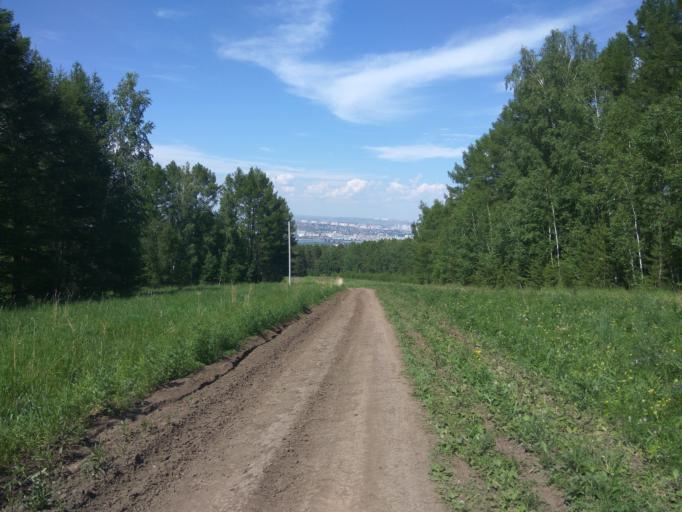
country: RU
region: Krasnoyarskiy
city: Krasnoyarsk
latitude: 55.9564
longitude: 92.8757
